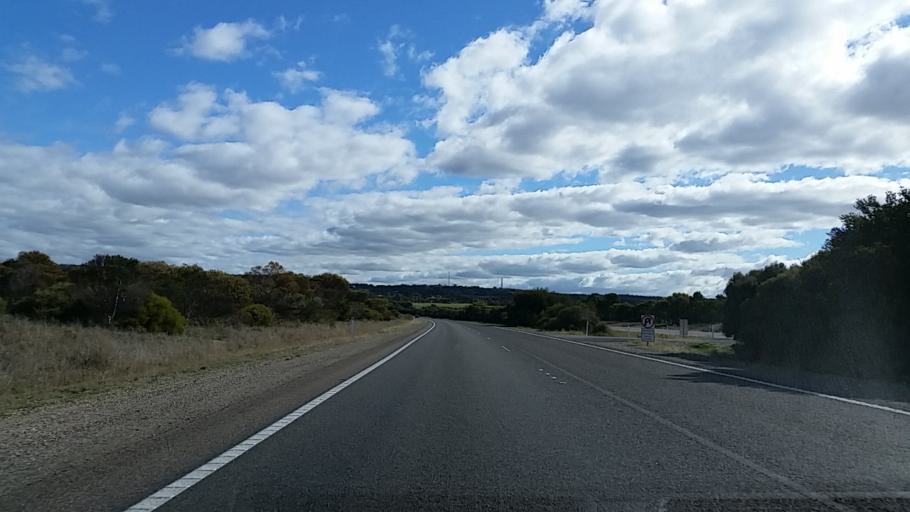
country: AU
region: South Australia
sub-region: Murray Bridge
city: Murray Bridge
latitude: -35.1447
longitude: 139.2506
